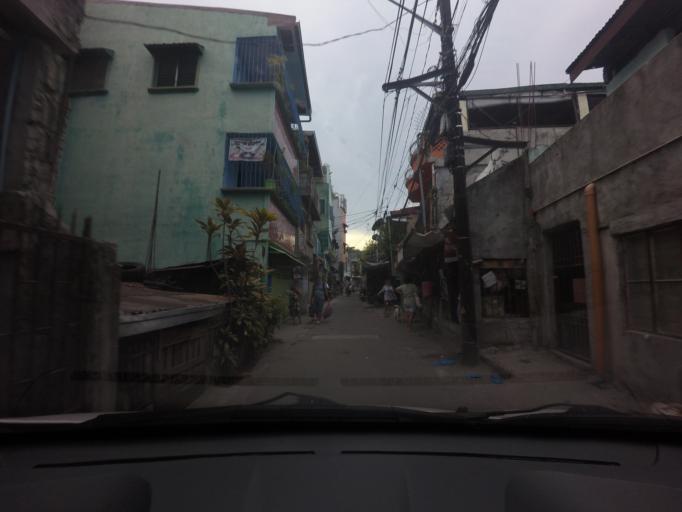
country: PH
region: Calabarzon
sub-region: Province of Rizal
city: Taguig
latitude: 14.4987
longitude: 121.0621
